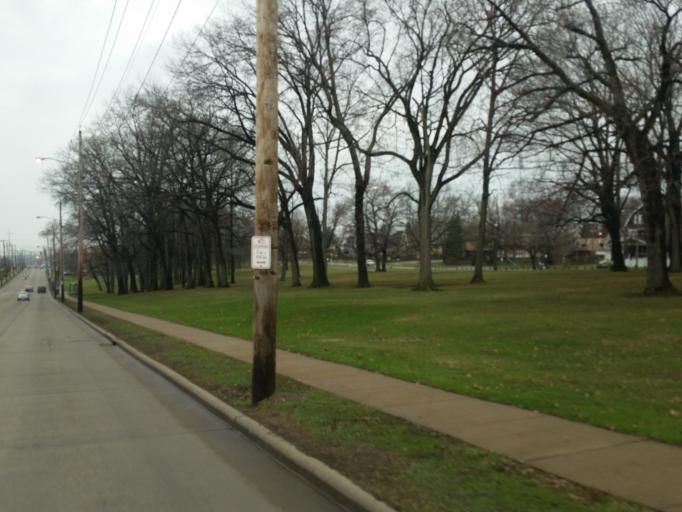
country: US
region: Ohio
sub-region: Cuyahoga County
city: Newburgh Heights
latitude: 41.4706
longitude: -81.6149
